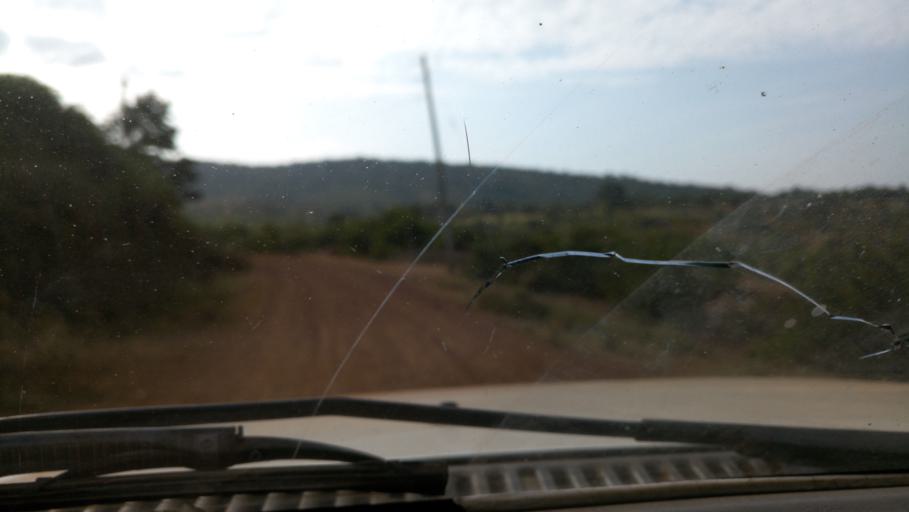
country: KE
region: Murang'a District
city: Karuri
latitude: -0.7104
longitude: 37.2118
